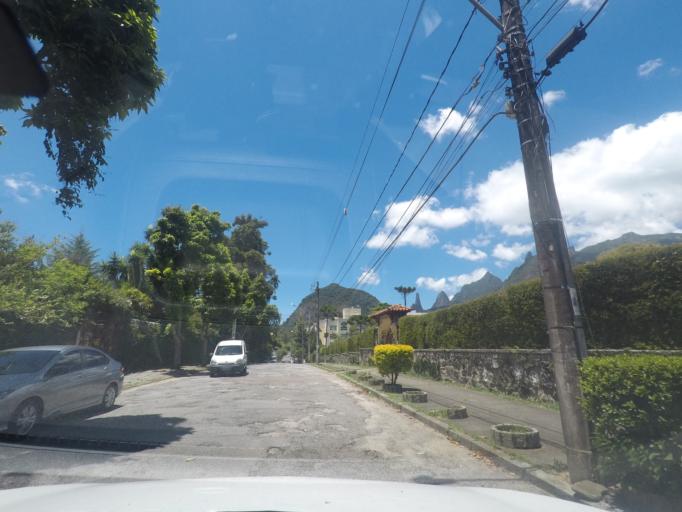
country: BR
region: Rio de Janeiro
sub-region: Teresopolis
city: Teresopolis
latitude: -22.4358
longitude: -42.9799
